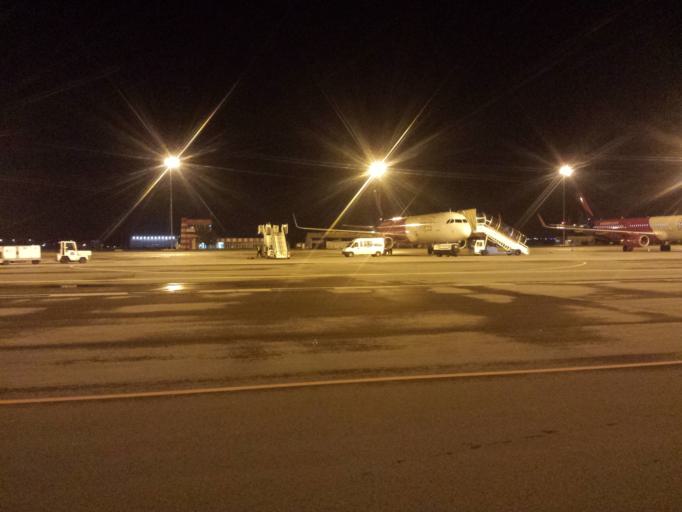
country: BG
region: Sofia-Capital
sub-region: Stolichna Obshtina
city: Sofia
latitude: 42.6898
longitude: 23.4035
